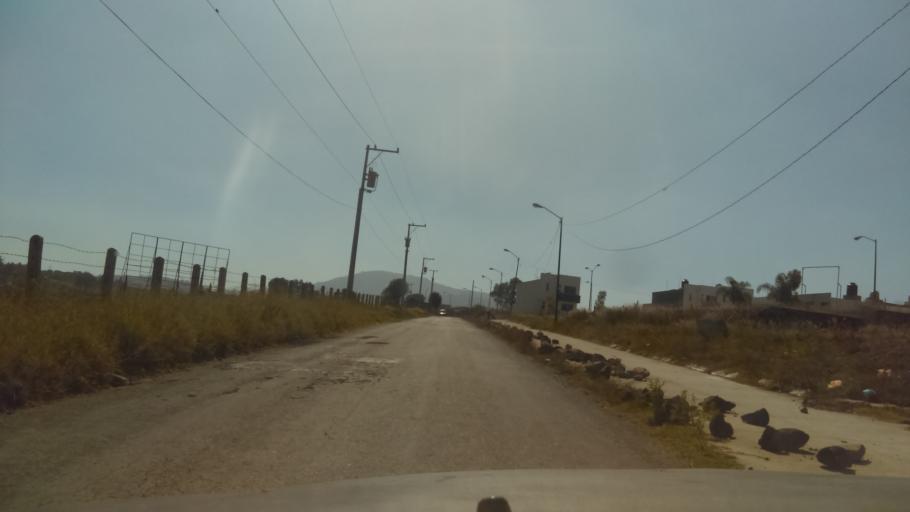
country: MX
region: Michoacan
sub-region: Morelia
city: Montana Monarca (Punta Altozano)
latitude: 19.6648
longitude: -101.1843
